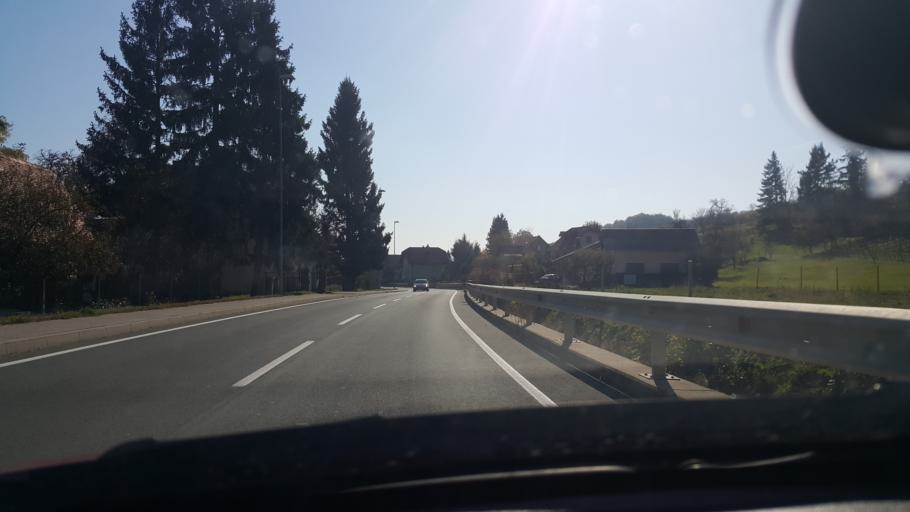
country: SI
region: Bistrica ob Sotli
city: Bistrica ob Sotli
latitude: 46.0218
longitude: 15.6904
